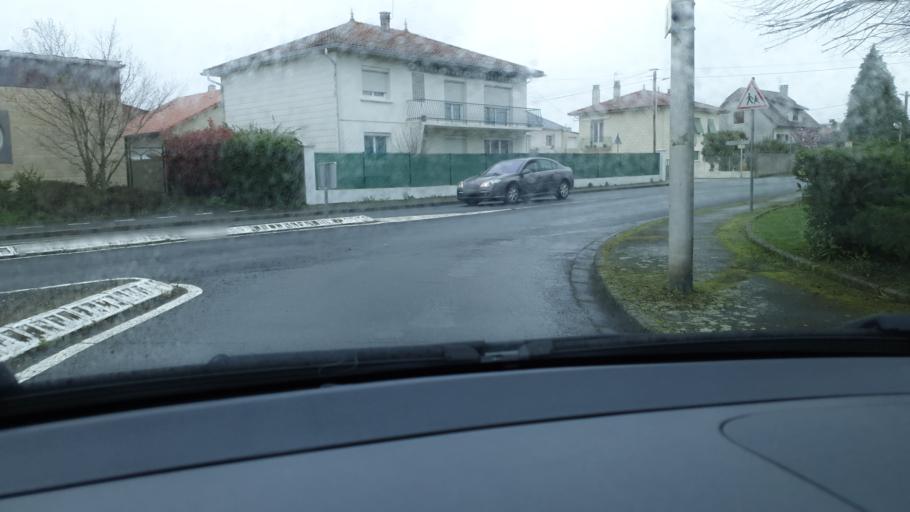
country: FR
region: Midi-Pyrenees
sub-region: Departement des Hautes-Pyrenees
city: Tarbes
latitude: 43.2413
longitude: 0.0512
